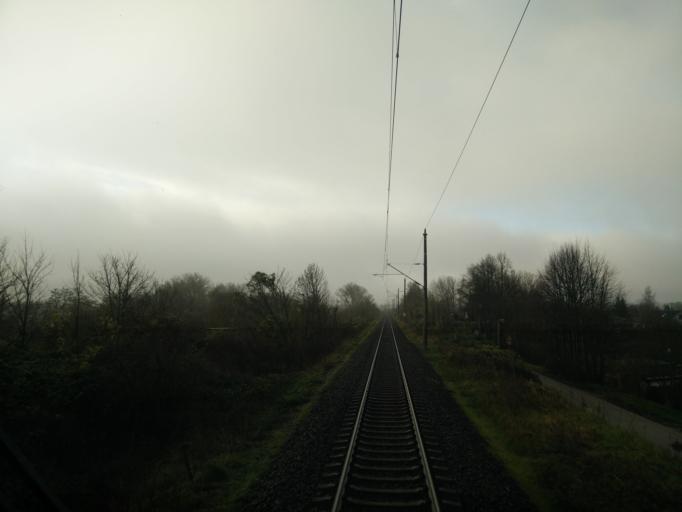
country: DE
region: Mecklenburg-Vorpommern
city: Wismar
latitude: 53.8728
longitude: 11.4693
